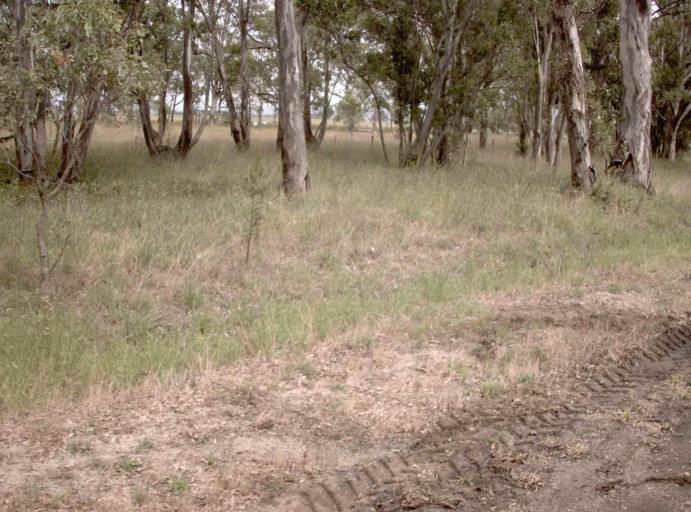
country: AU
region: Victoria
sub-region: Wellington
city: Sale
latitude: -37.9087
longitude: 147.0792
